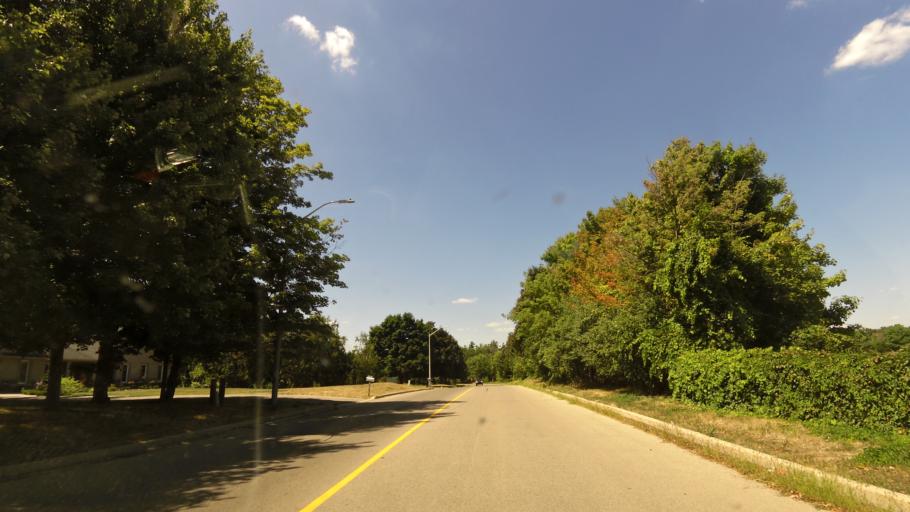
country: CA
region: Ontario
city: Brampton
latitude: 43.6424
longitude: -79.8687
